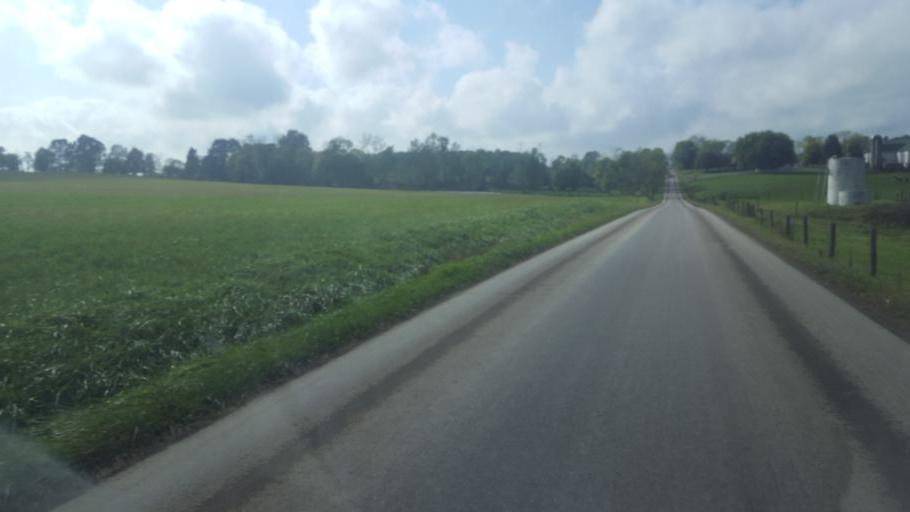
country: US
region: Ohio
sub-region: Wayne County
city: Apple Creek
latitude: 40.6460
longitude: -81.8133
